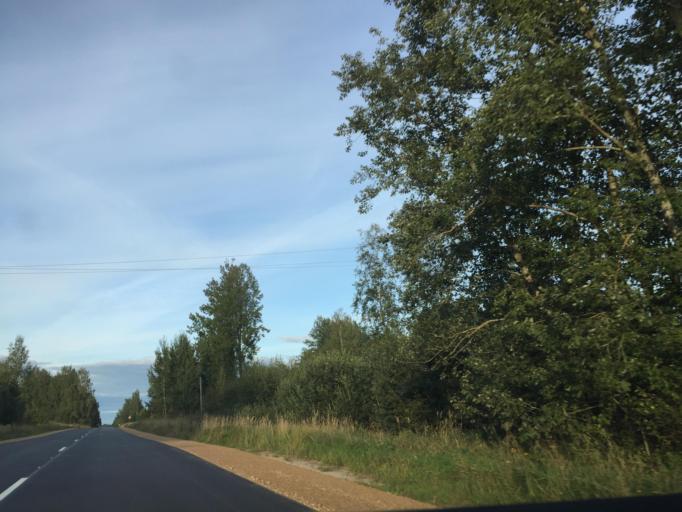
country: LV
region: Viesite
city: Viesite
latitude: 56.3511
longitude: 25.5910
